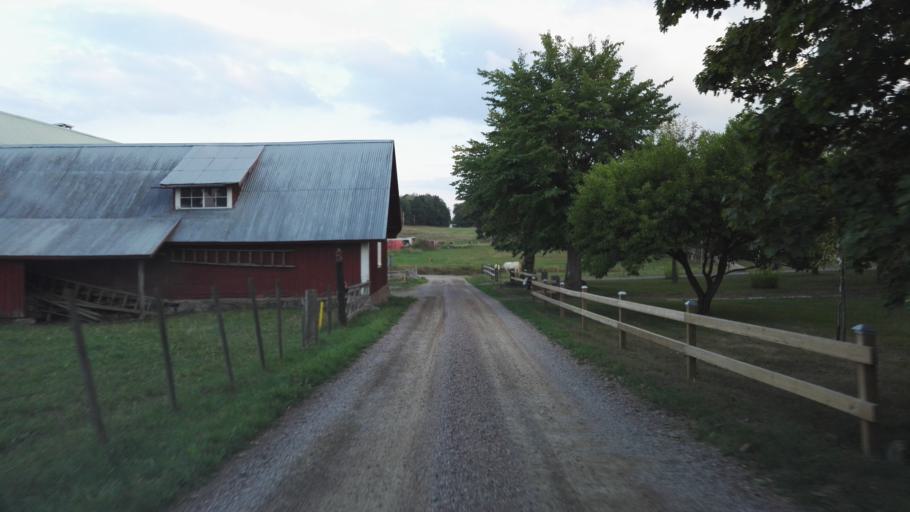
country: SE
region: Joenkoeping
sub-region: Vetlanda Kommun
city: Landsbro
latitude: 57.2192
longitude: 14.9005
